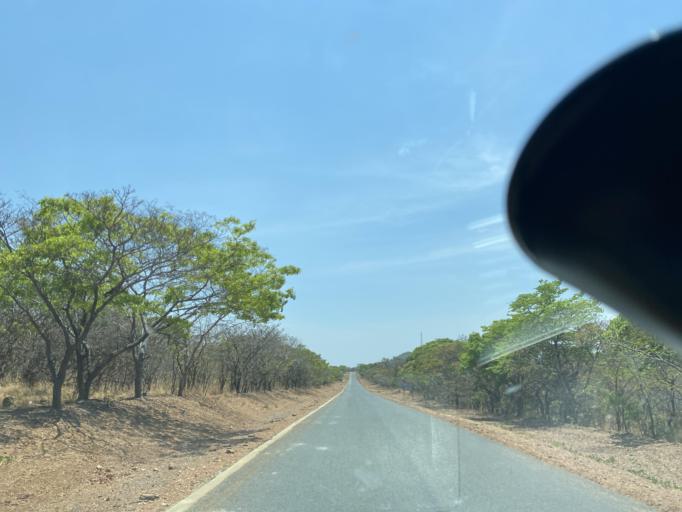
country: ZM
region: Lusaka
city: Kafue
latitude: -15.8493
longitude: 28.4159
